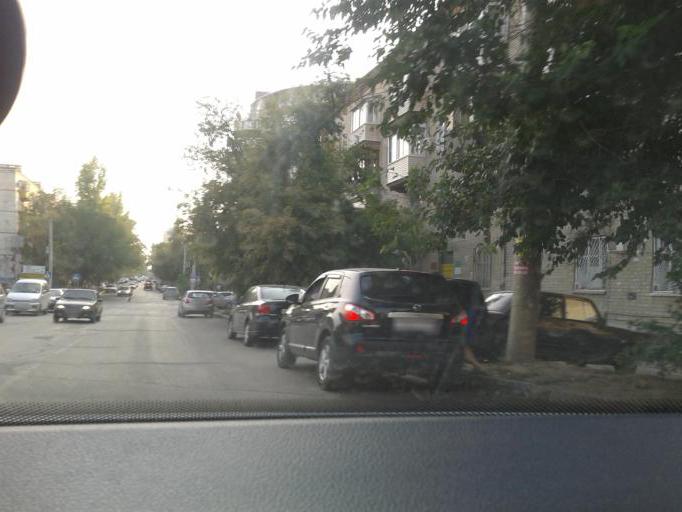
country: RU
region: Volgograd
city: Volgograd
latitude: 48.7019
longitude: 44.5018
